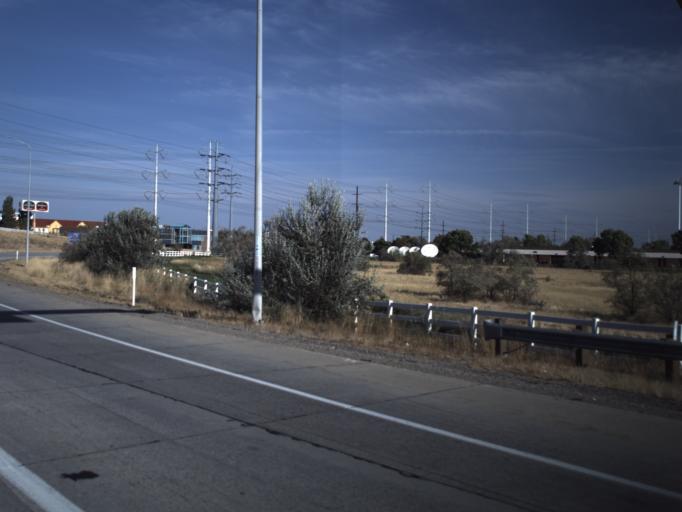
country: US
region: Utah
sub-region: Salt Lake County
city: West Valley City
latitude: 40.7695
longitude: -112.0035
